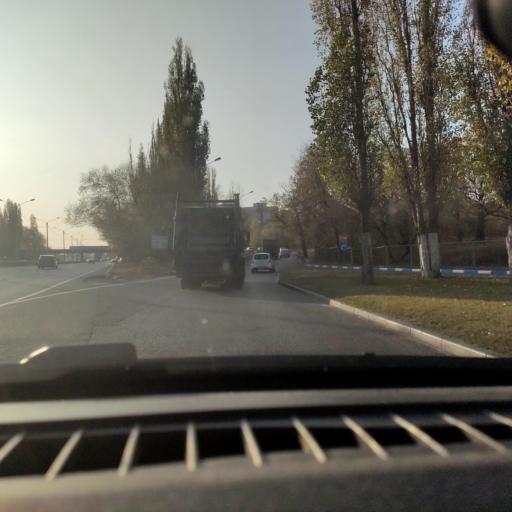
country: RU
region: Voronezj
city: Voronezh
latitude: 51.6634
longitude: 39.1290
